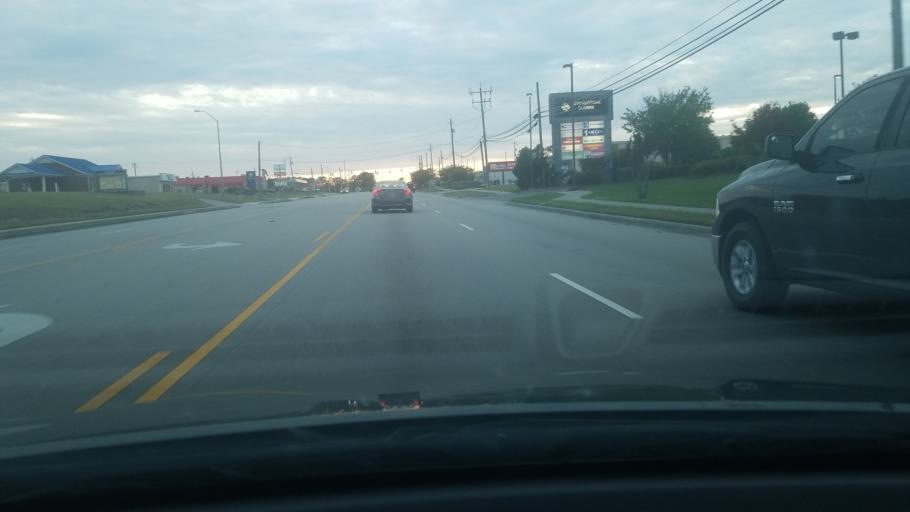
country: US
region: North Carolina
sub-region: Onslow County
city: Swansboro
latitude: 34.6921
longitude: -77.1278
